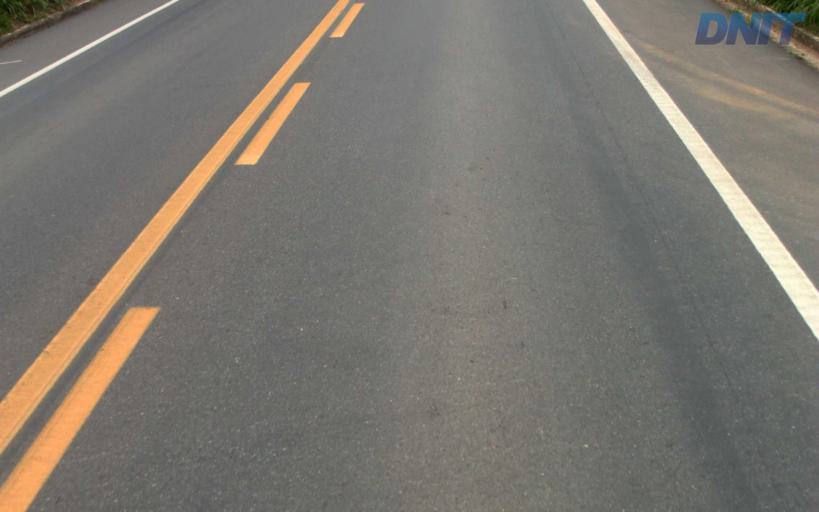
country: BR
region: Minas Gerais
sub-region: Governador Valadares
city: Governador Valadares
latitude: -18.9404
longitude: -42.0576
